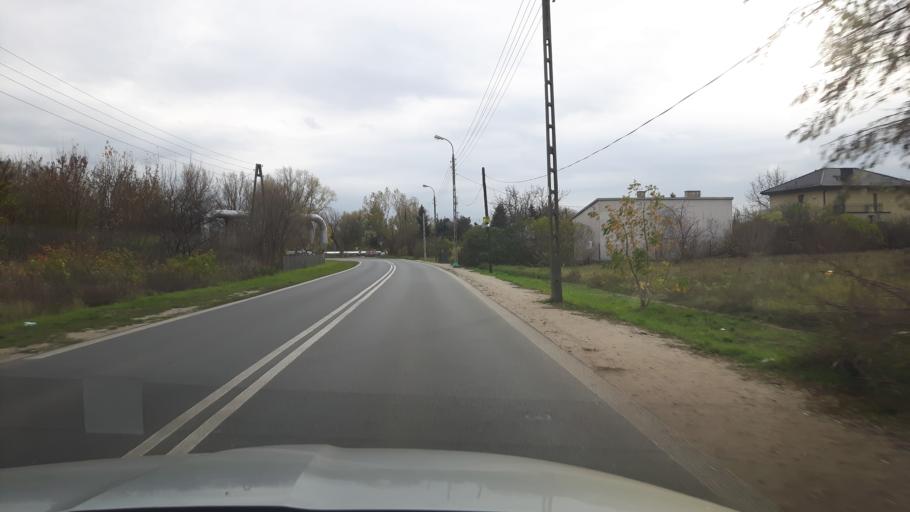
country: PL
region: Masovian Voivodeship
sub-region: Powiat wolominski
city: Zabki
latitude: 52.2761
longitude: 21.0881
